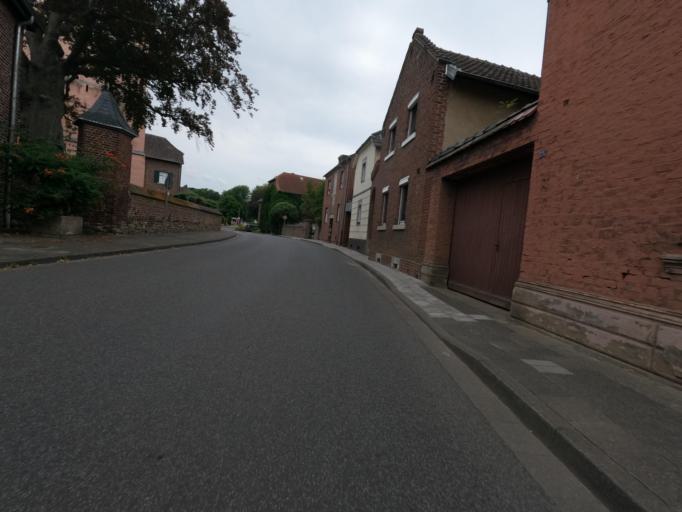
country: DE
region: North Rhine-Westphalia
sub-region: Regierungsbezirk Koln
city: Aldenhoven
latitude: 50.9421
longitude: 6.3040
